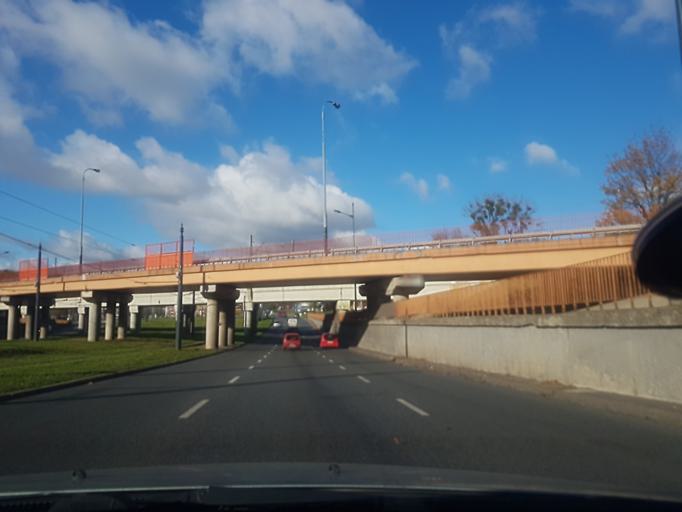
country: PL
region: Lodz Voivodeship
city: Lodz
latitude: 51.7637
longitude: 19.5214
